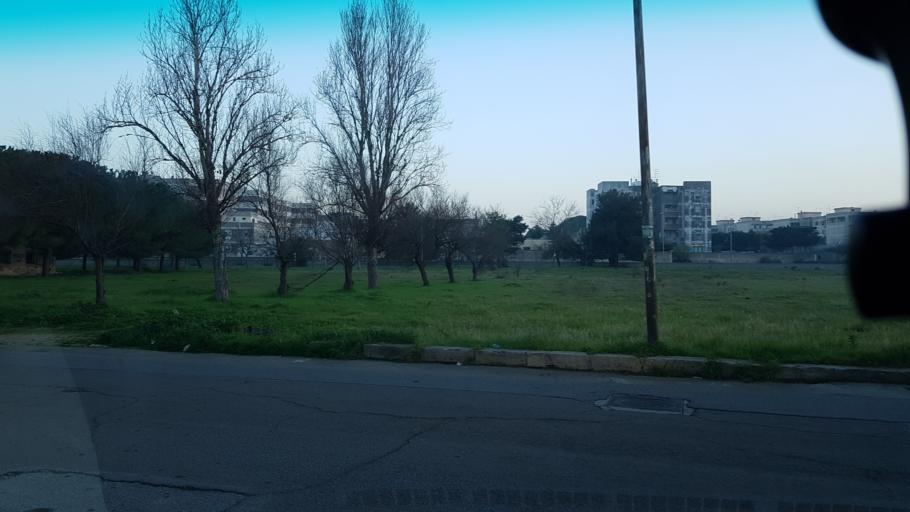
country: IT
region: Apulia
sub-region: Provincia di Brindisi
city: Mesagne
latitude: 40.5617
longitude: 17.7955
